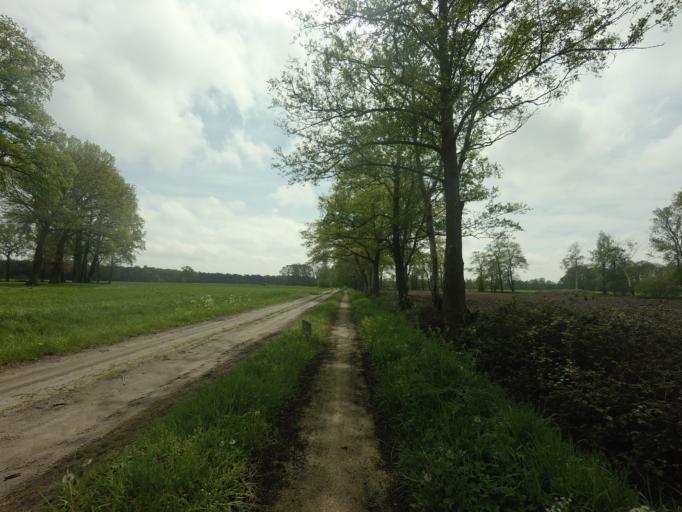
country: NL
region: Overijssel
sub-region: Gemeente Haaksbergen
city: Haaksbergen
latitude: 52.1322
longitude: 6.7402
